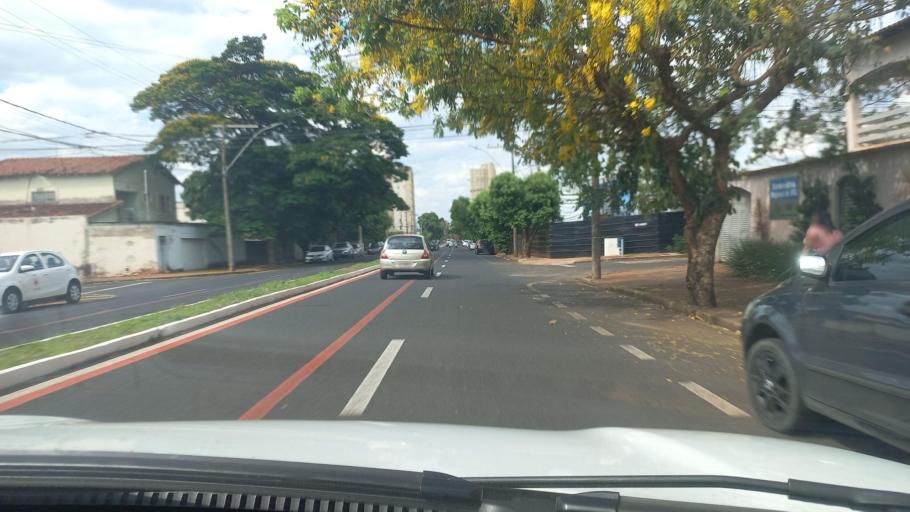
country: BR
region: Minas Gerais
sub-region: Uberaba
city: Uberaba
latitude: -19.7636
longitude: -47.9599
